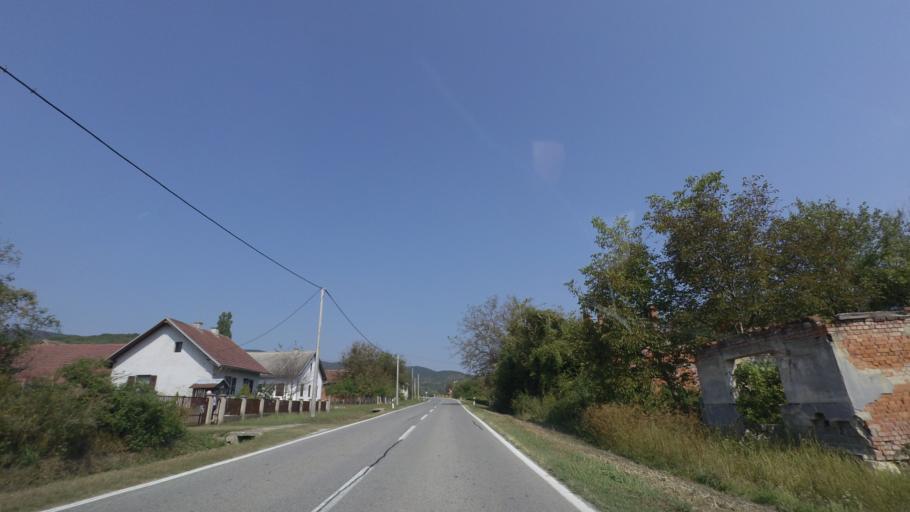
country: HR
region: Brodsko-Posavska
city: Resetari
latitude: 45.4008
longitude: 17.5032
